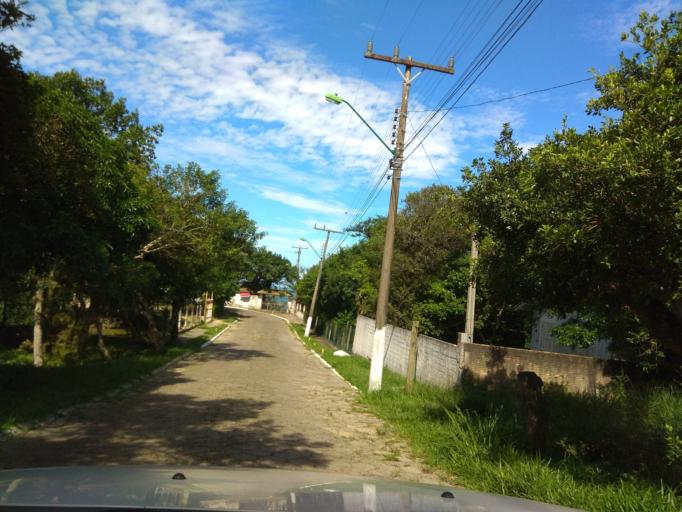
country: BR
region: Santa Catarina
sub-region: Laguna
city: Laguna
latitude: -28.4862
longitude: -48.7765
